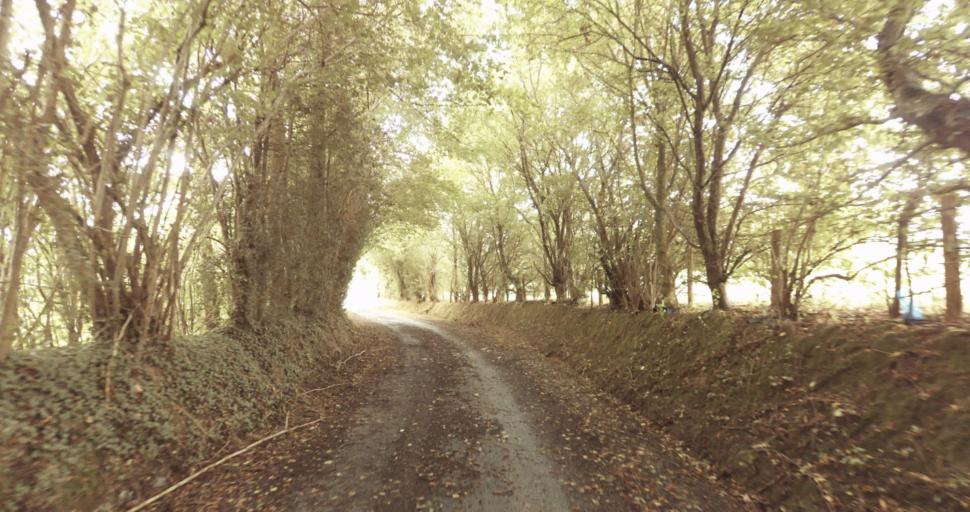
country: FR
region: Lower Normandy
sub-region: Departement de l'Orne
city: Sainte-Gauburge-Sainte-Colombe
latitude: 48.7084
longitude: 0.3924
